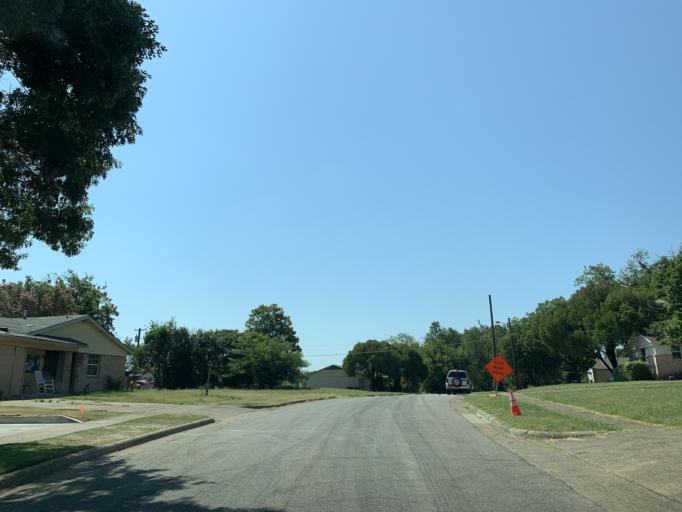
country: US
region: Texas
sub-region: Dallas County
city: Hutchins
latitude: 32.6733
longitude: -96.7552
